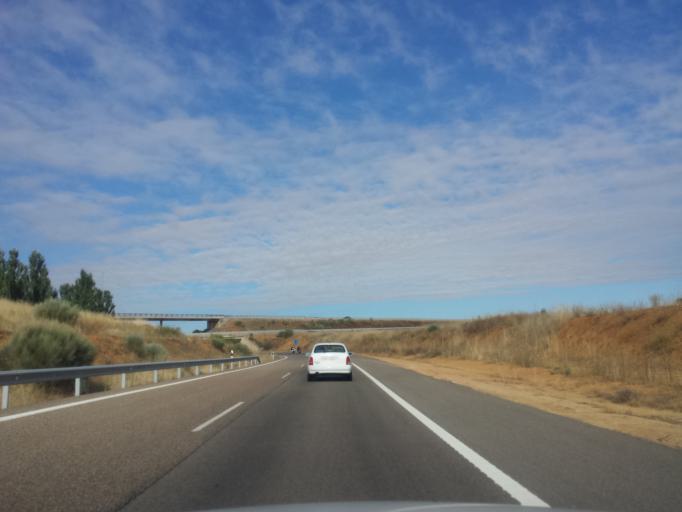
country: ES
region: Castille and Leon
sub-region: Provincia de Leon
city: Onzonilla
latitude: 42.5048
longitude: -5.5942
